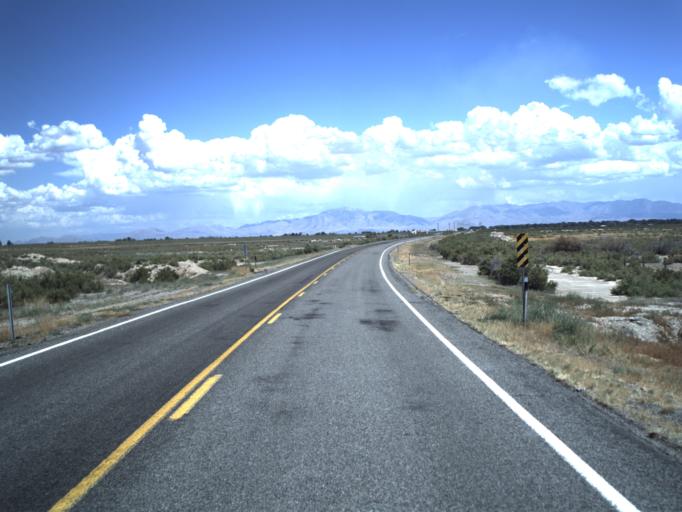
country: US
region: Utah
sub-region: Millard County
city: Delta
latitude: 39.3307
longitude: -112.7177
